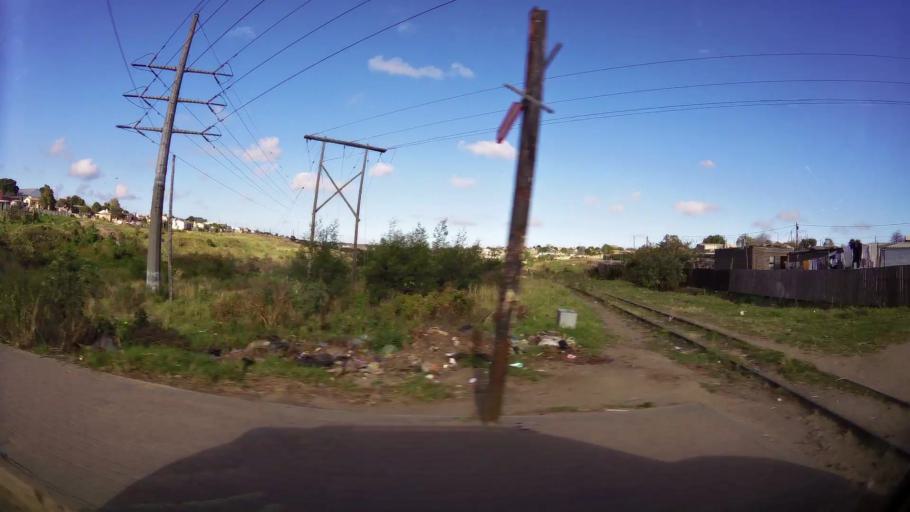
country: ZA
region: Western Cape
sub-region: Eden District Municipality
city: George
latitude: -33.9803
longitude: 22.4760
